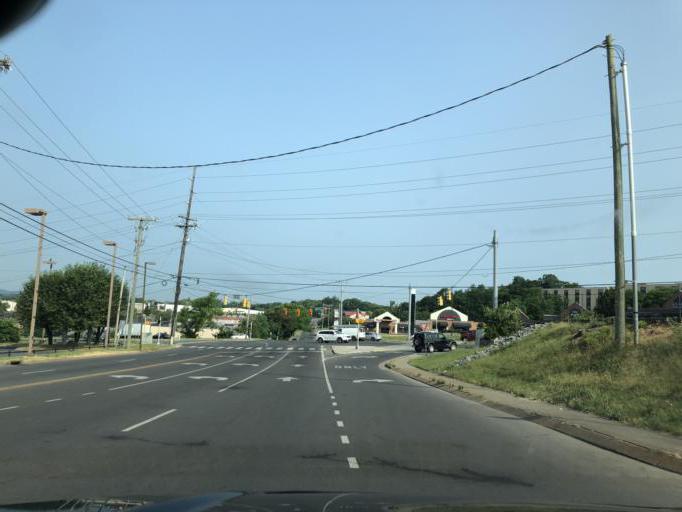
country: US
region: Tennessee
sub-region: Rutherford County
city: La Vergne
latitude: 36.0494
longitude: -86.6488
